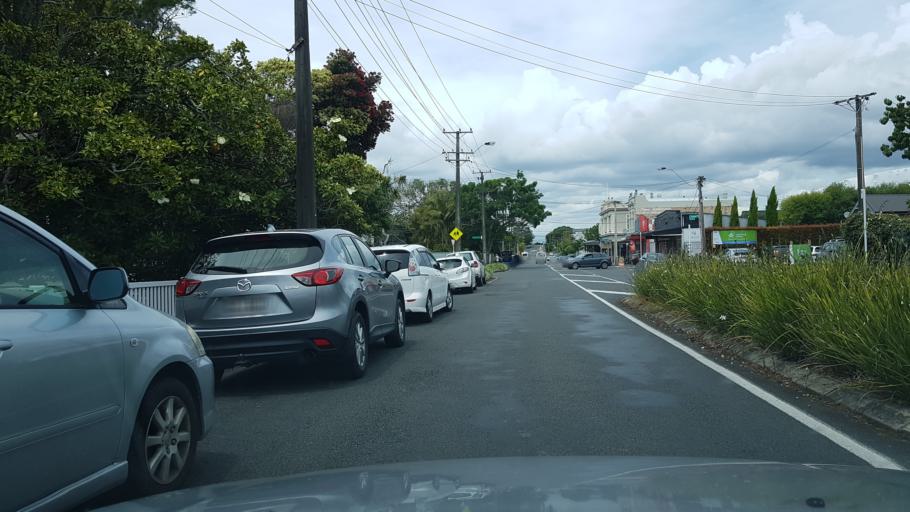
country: NZ
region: Auckland
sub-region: Auckland
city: North Shore
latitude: -36.8159
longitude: 174.7317
